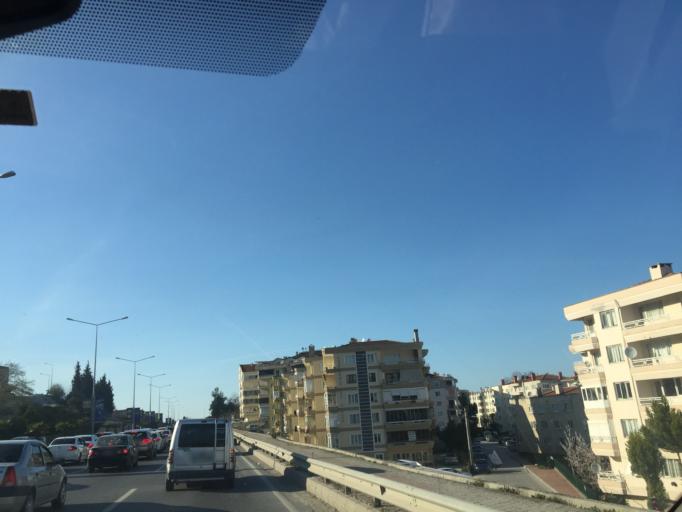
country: TR
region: Bursa
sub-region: Mudanya
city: Mudanya
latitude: 40.3597
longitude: 28.9106
